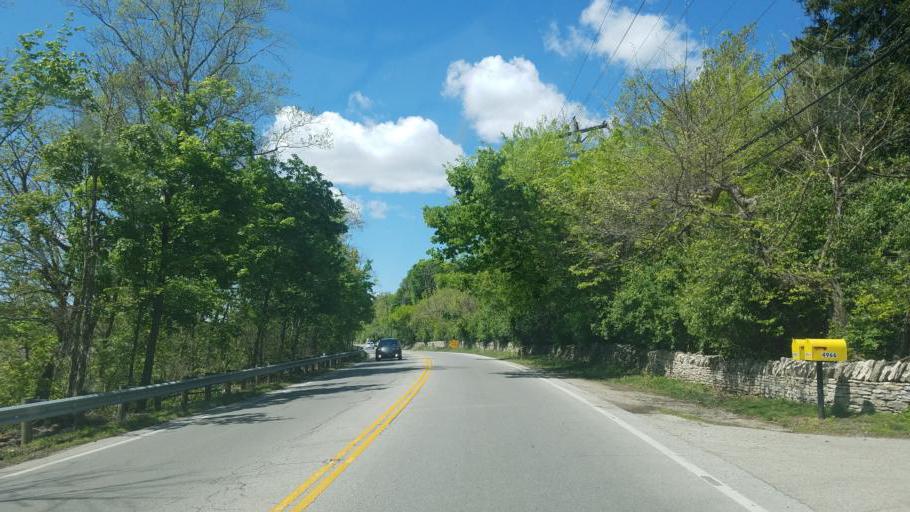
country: US
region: Ohio
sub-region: Franklin County
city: Dublin
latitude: 40.0535
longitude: -83.0961
